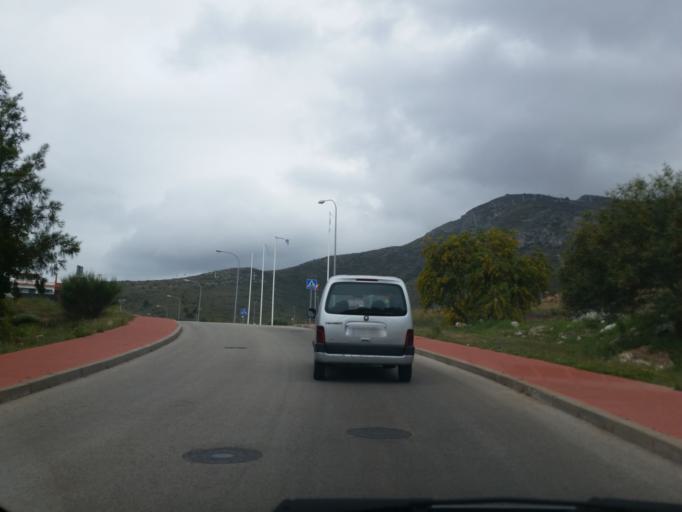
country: ES
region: Andalusia
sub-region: Provincia de Malaga
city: Benalmadena
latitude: 36.6122
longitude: -4.5412
